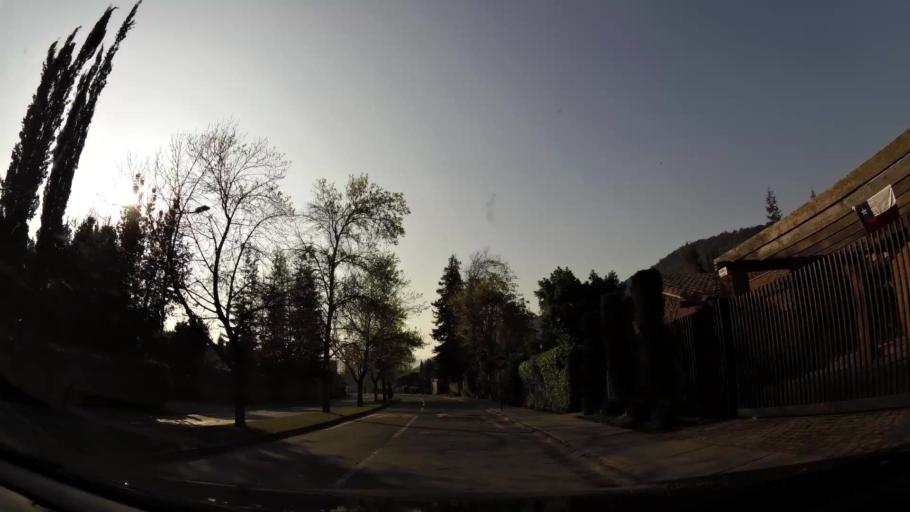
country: CL
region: Santiago Metropolitan
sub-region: Provincia de Santiago
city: Villa Presidente Frei, Nunoa, Santiago, Chile
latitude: -33.3533
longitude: -70.5327
